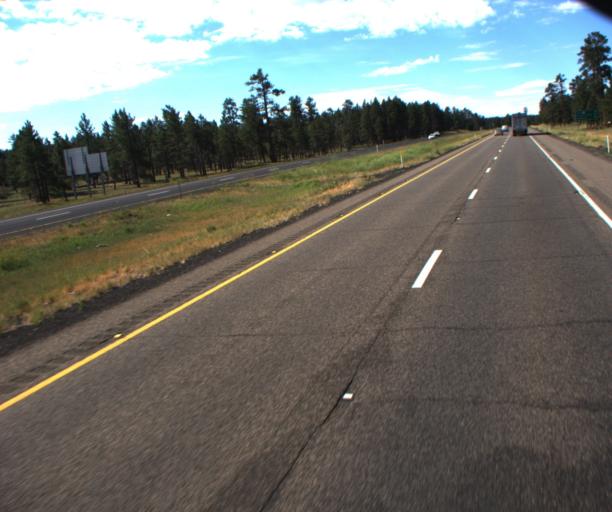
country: US
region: Arizona
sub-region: Coconino County
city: Sedona
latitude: 34.8422
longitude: -111.6039
